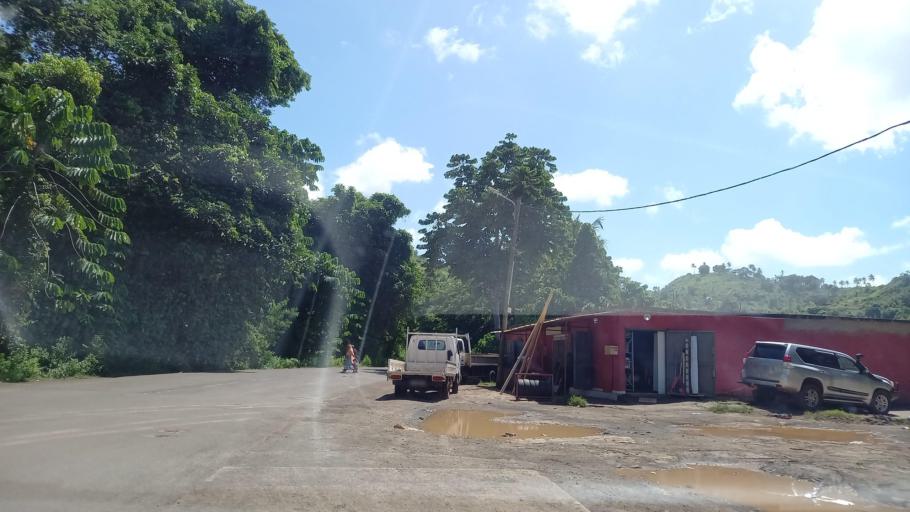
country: YT
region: Bandraboua
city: Bandraboua
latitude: -12.7252
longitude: 45.1233
